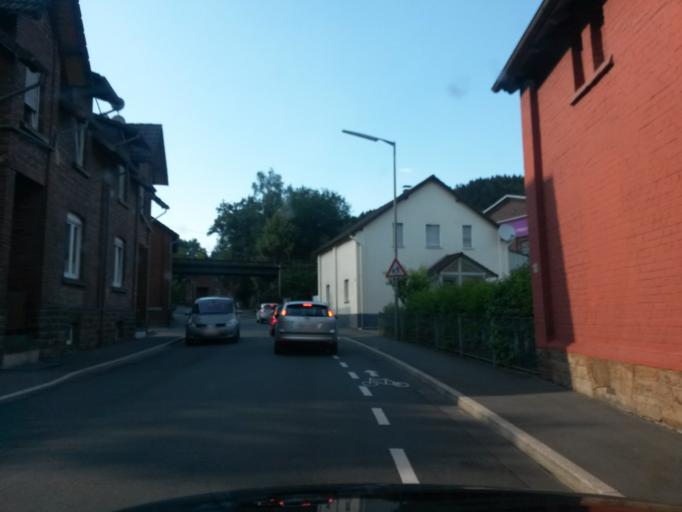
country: DE
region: North Rhine-Westphalia
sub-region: Regierungsbezirk Koln
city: Gummersbach
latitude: 50.9903
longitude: 7.5535
